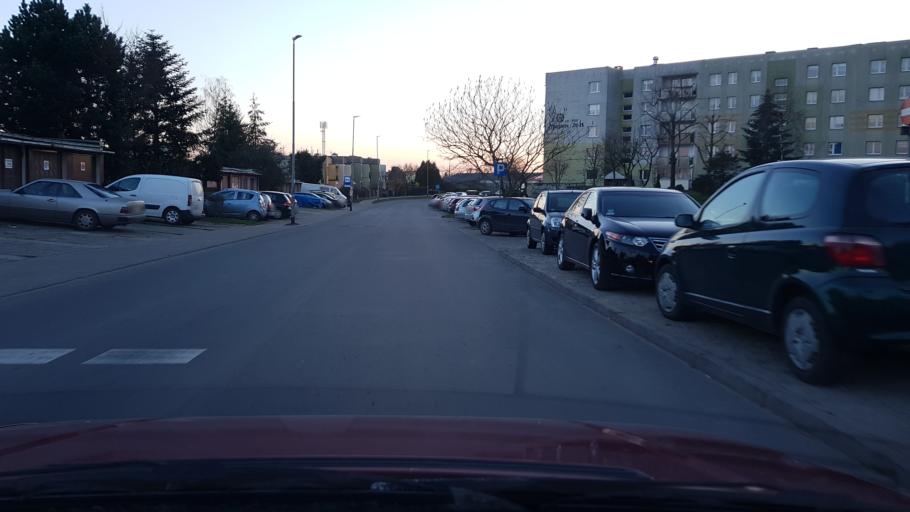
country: PL
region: West Pomeranian Voivodeship
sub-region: Szczecin
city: Szczecin
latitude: 53.4619
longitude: 14.5579
